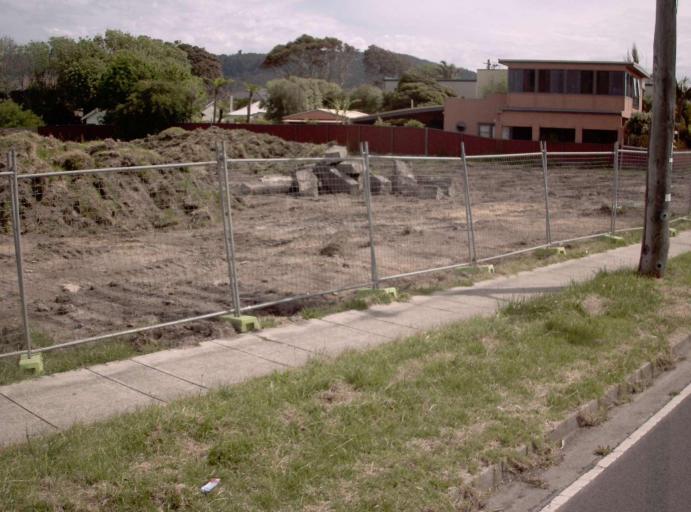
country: AU
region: Victoria
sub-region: Mornington Peninsula
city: Dromana
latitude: -38.3284
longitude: 144.9740
